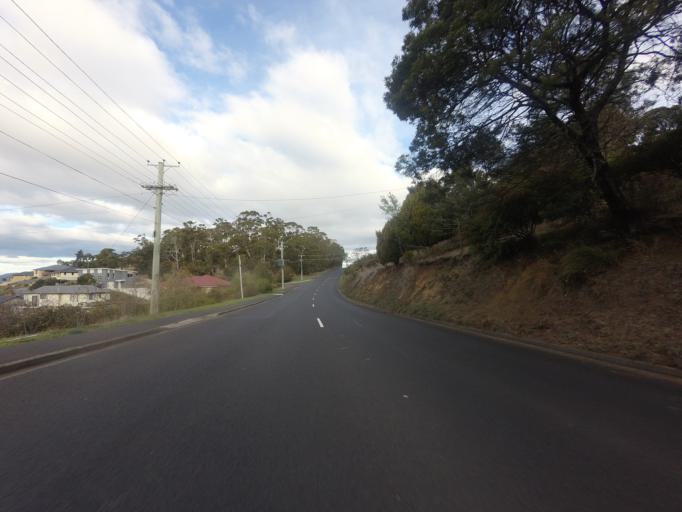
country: AU
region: Tasmania
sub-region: Glenorchy
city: Berriedale
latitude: -42.8181
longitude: 147.2435
